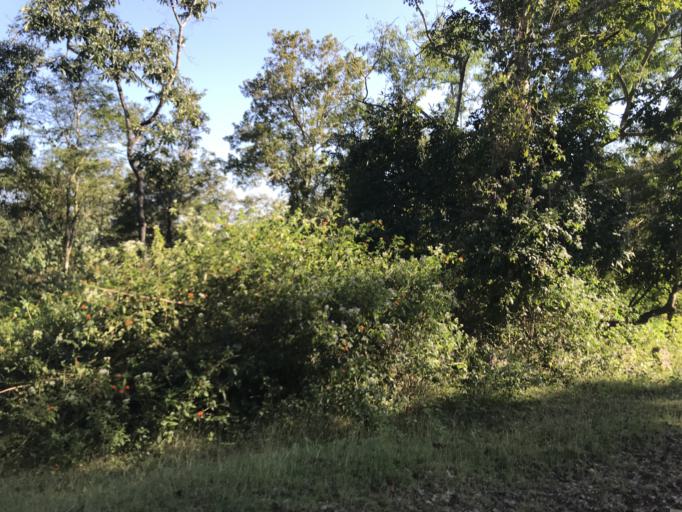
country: IN
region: Karnataka
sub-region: Mysore
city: Heggadadevankote
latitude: 11.9657
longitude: 76.2434
